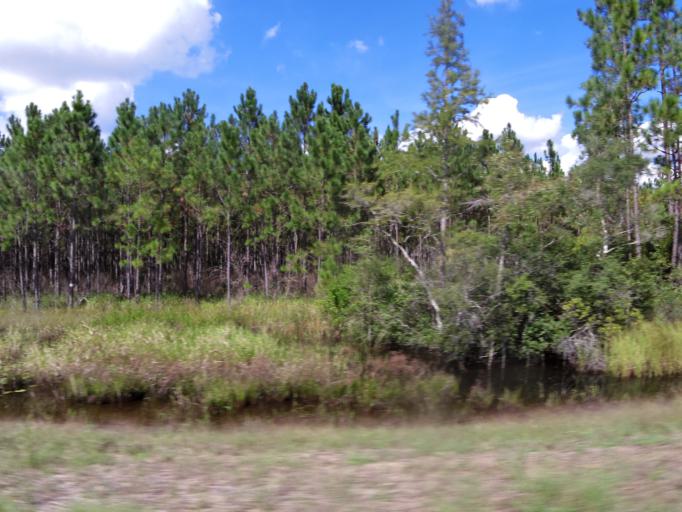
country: US
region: Florida
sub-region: Hamilton County
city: Jasper
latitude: 30.6743
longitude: -82.6726
